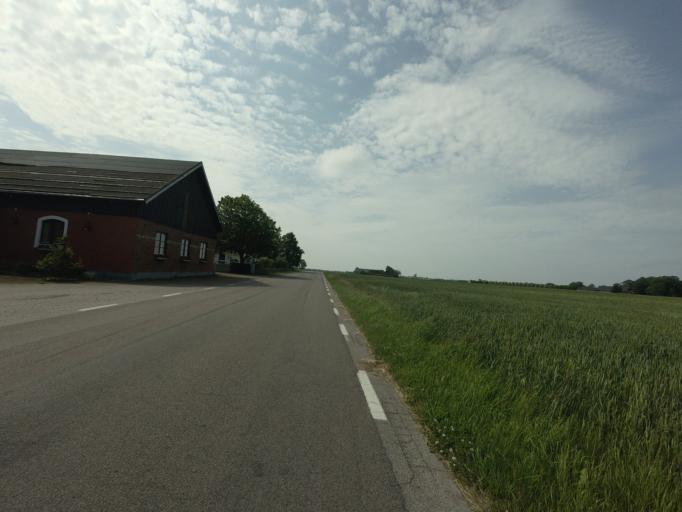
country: SE
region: Skane
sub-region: Helsingborg
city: Odakra
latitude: 56.1981
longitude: 12.6987
